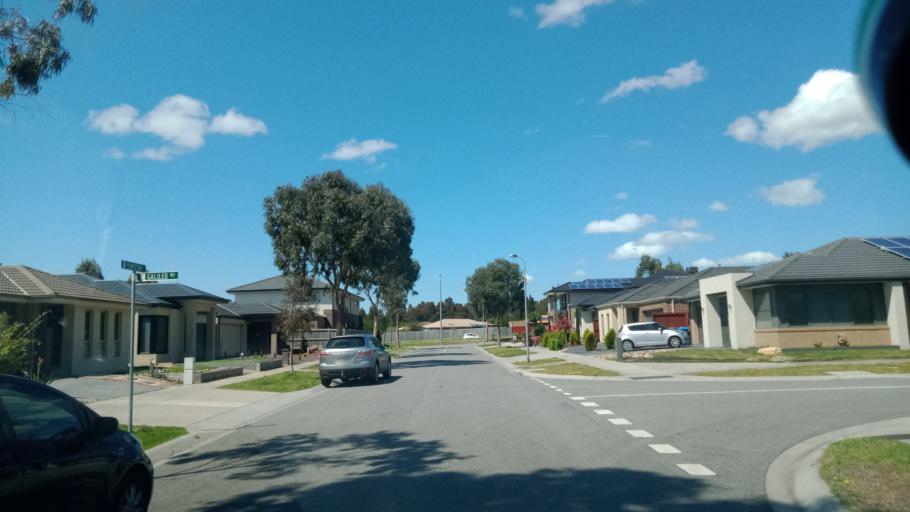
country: AU
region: Victoria
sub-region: Casey
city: Cranbourne West
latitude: -38.0964
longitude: 145.2536
